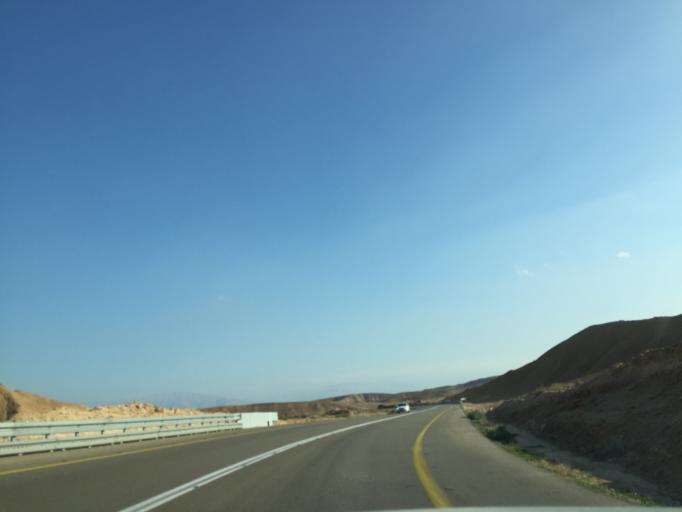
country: IL
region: Southern District
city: `En Boqeq
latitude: 31.1814
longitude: 35.2926
